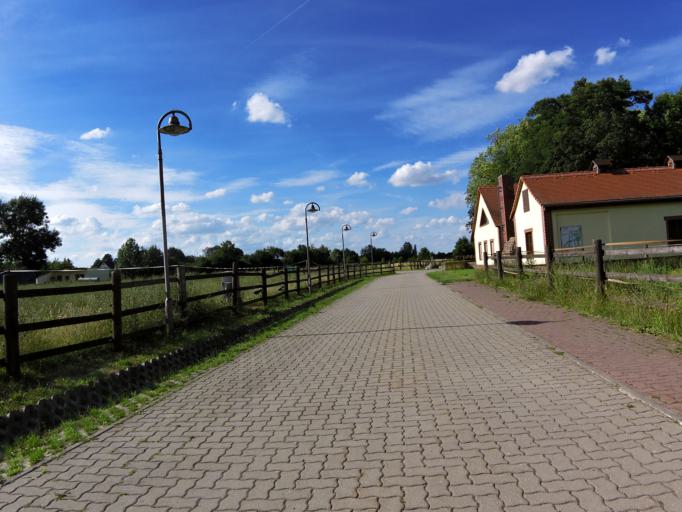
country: DE
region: Saxony
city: Taucha
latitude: 51.3262
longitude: 12.4499
